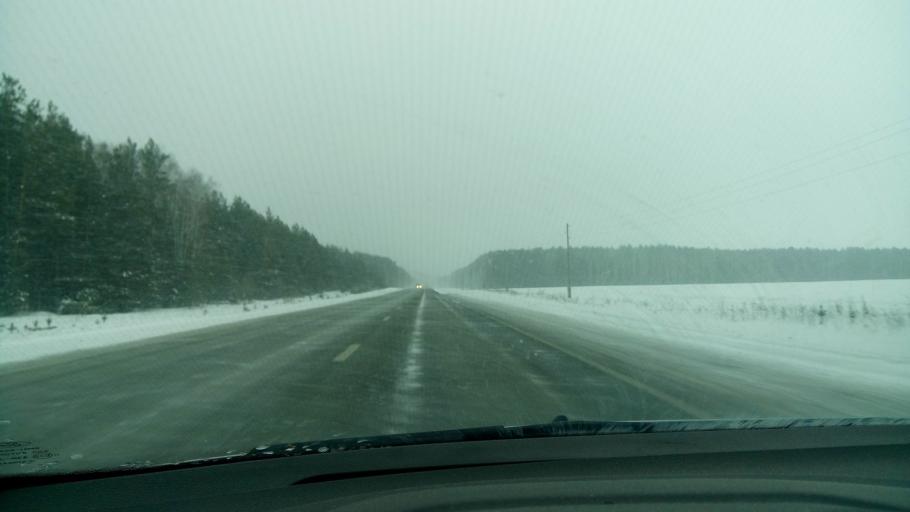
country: RU
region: Sverdlovsk
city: Gryaznovskoye
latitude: 56.7847
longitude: 61.6632
